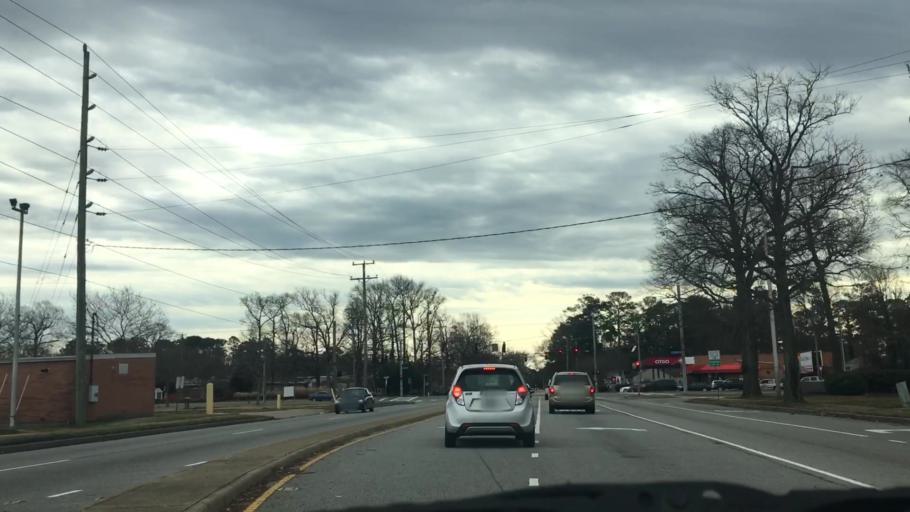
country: US
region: Virginia
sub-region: City of Norfolk
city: Norfolk
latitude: 36.8555
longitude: -76.2403
